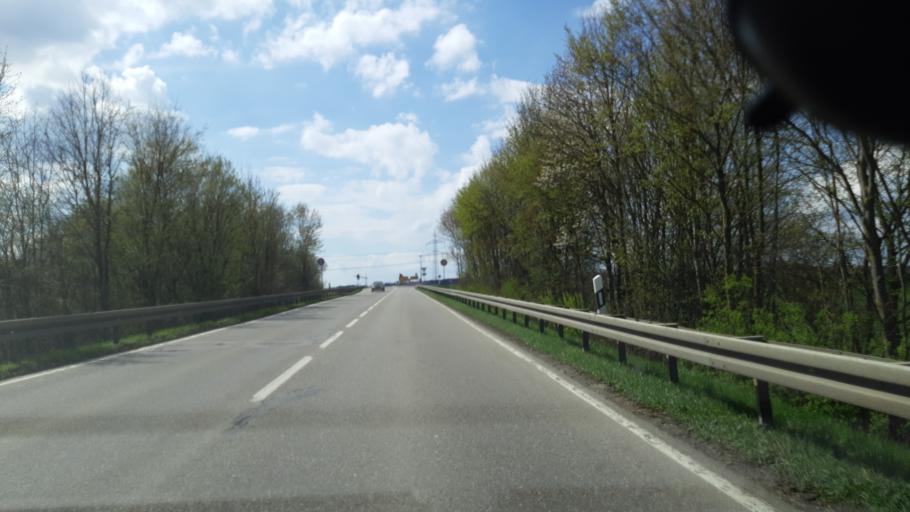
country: DE
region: Baden-Wuerttemberg
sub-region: Regierungsbezirk Stuttgart
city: Westhausen
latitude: 48.8075
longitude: 10.1974
